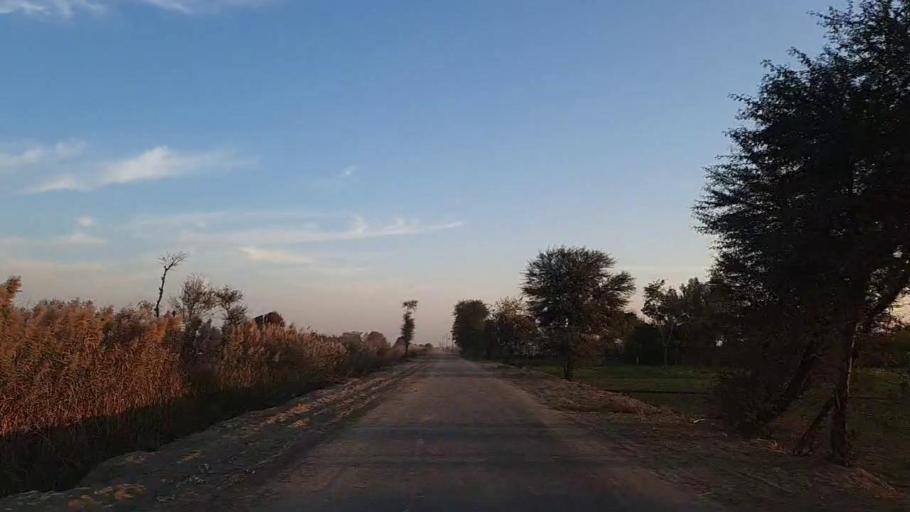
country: PK
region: Sindh
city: Bandhi
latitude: 26.6268
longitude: 68.3707
